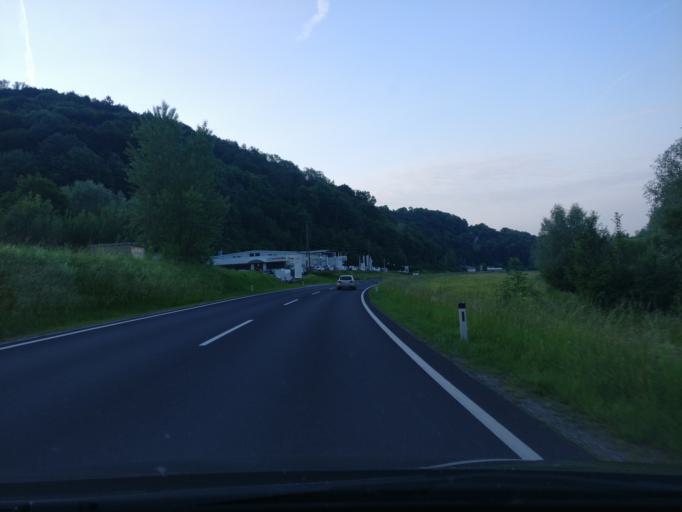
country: AT
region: Upper Austria
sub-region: Politischer Bezirk Urfahr-Umgebung
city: Steyregg
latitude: 48.3034
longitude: 14.3395
